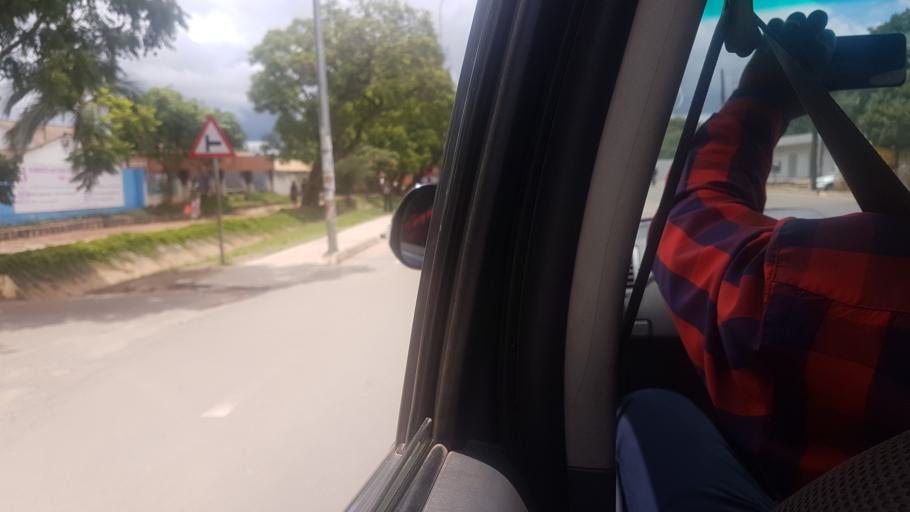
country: ZM
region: Lusaka
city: Lusaka
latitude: -15.4347
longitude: 28.3088
